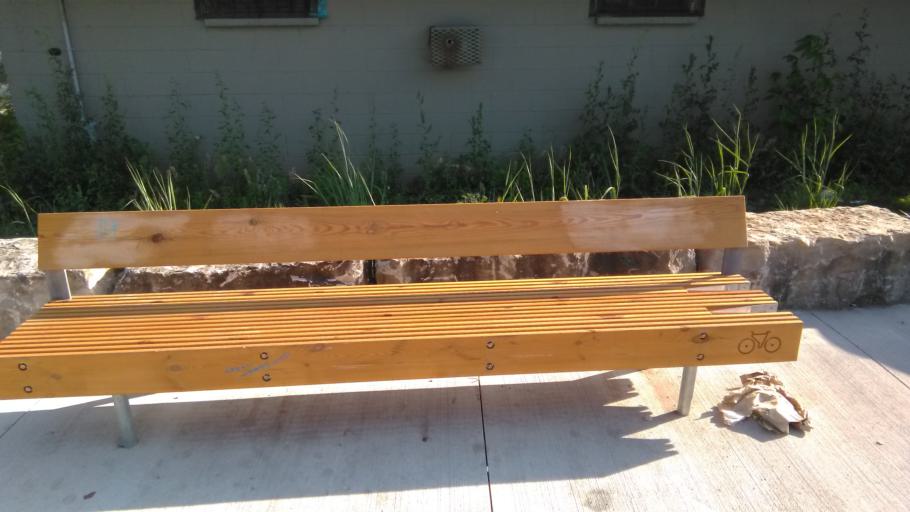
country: CA
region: Ontario
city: Kitchener
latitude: 43.4440
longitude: -80.5037
